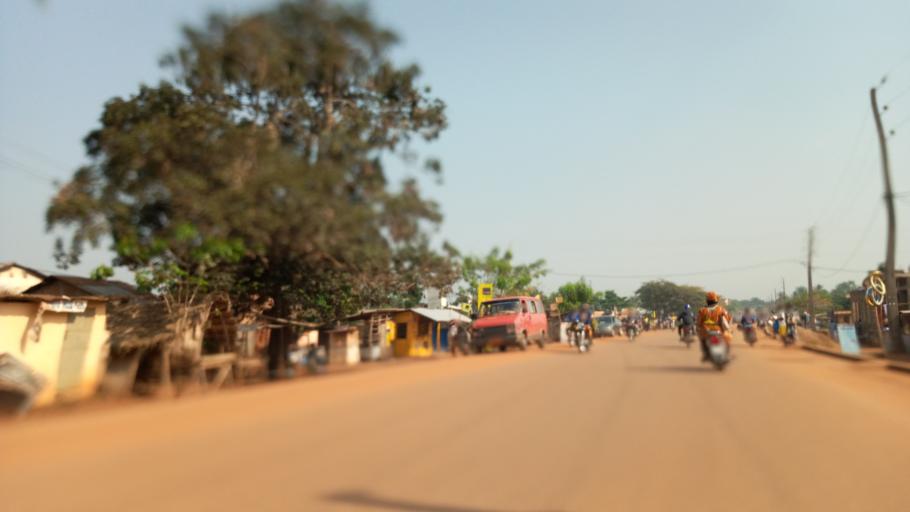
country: BJ
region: Queme
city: Porto-Novo
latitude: 6.5338
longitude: 2.6483
